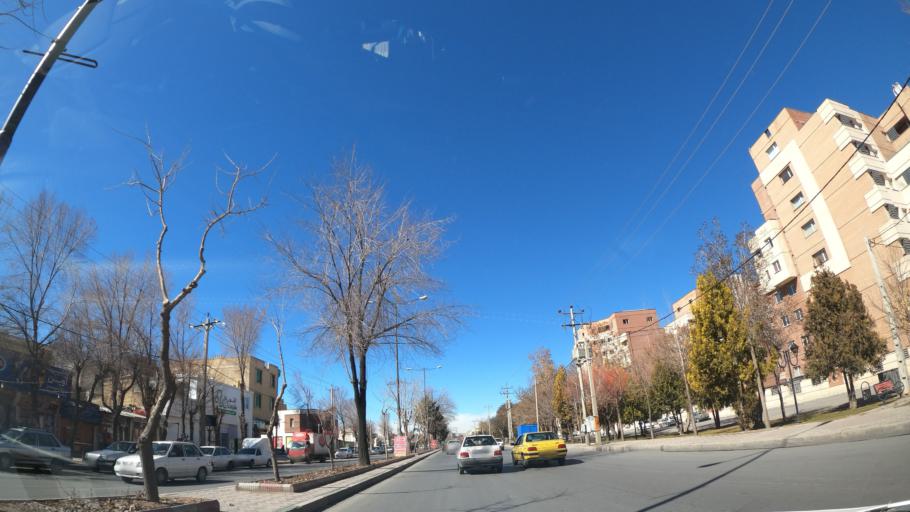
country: IR
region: Chahar Mahall va Bakhtiari
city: Shahrekord
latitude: 32.3135
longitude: 50.8774
